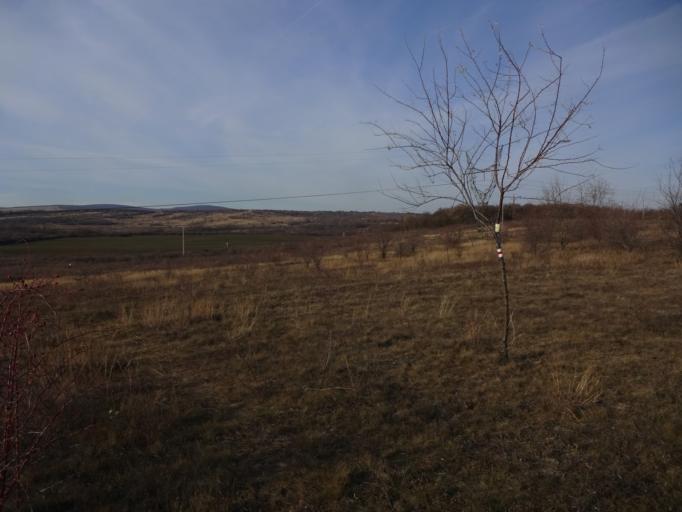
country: HU
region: Veszprem
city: Varpalota
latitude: 47.2221
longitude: 18.1942
